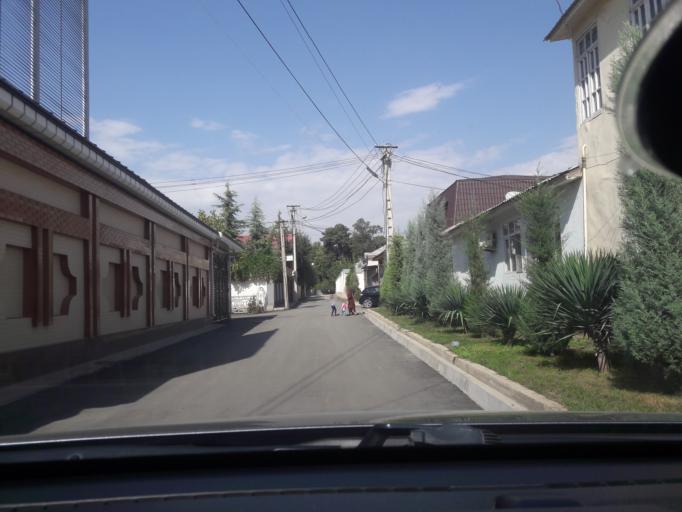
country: TJ
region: Dushanbe
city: Dushanbe
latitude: 38.5761
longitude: 68.7969
